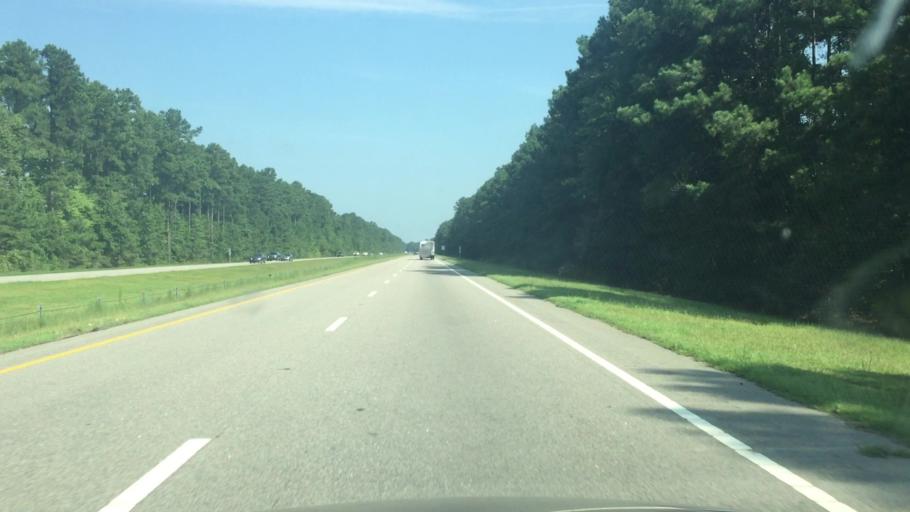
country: US
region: North Carolina
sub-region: Robeson County
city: Lumberton
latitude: 34.5458
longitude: -79.0218
